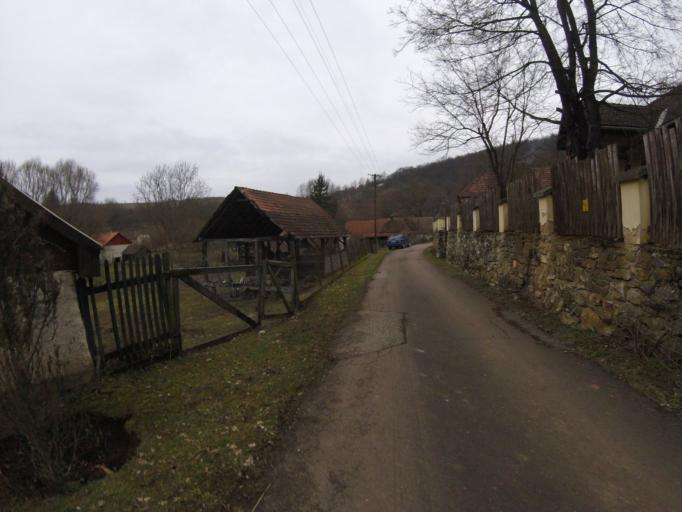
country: HU
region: Borsod-Abauj-Zemplen
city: Rudabanya
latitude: 48.4469
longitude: 20.6047
